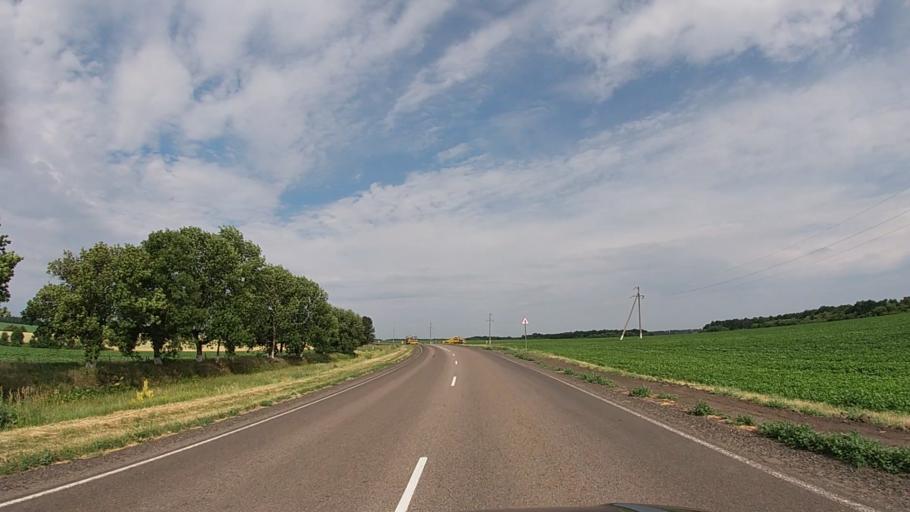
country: RU
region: Belgorod
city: Krasnaya Yaruga
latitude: 50.8078
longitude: 35.5412
